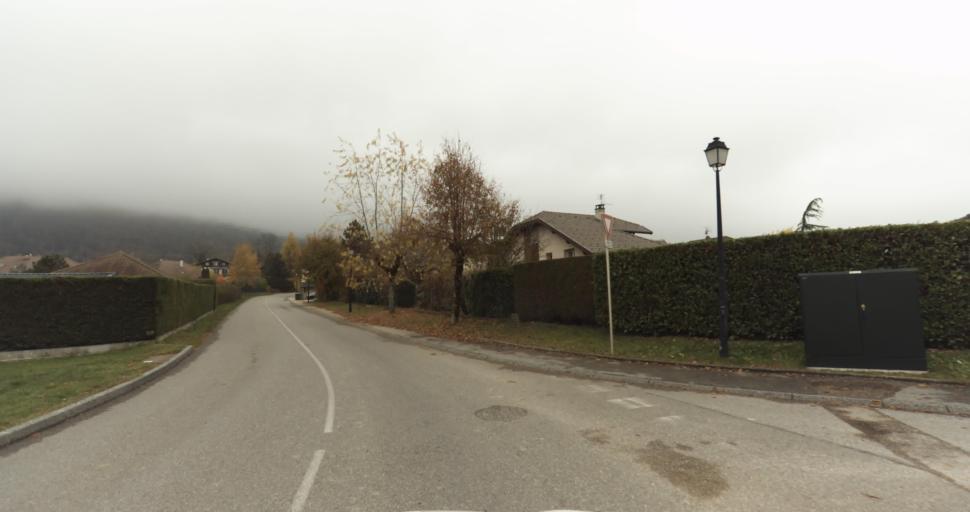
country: FR
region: Rhone-Alpes
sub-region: Departement de la Haute-Savoie
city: Viuz-la-Chiesaz
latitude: 45.8436
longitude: 6.0839
